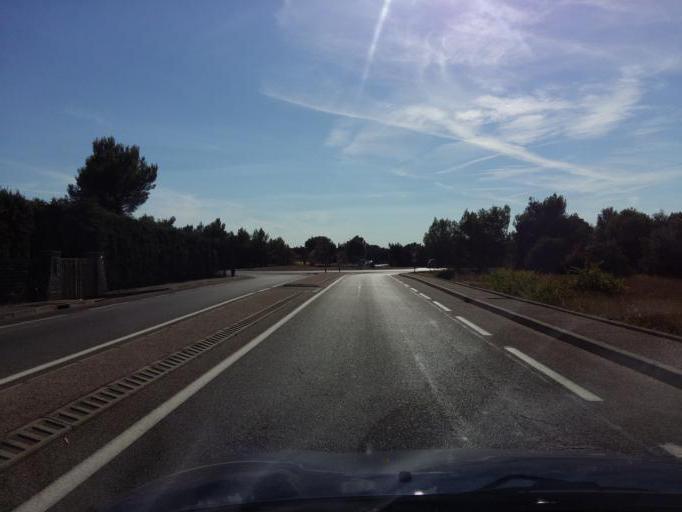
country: FR
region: Provence-Alpes-Cote d'Azur
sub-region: Departement du Vaucluse
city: Saint-Didier
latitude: 44.0218
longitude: 5.0963
